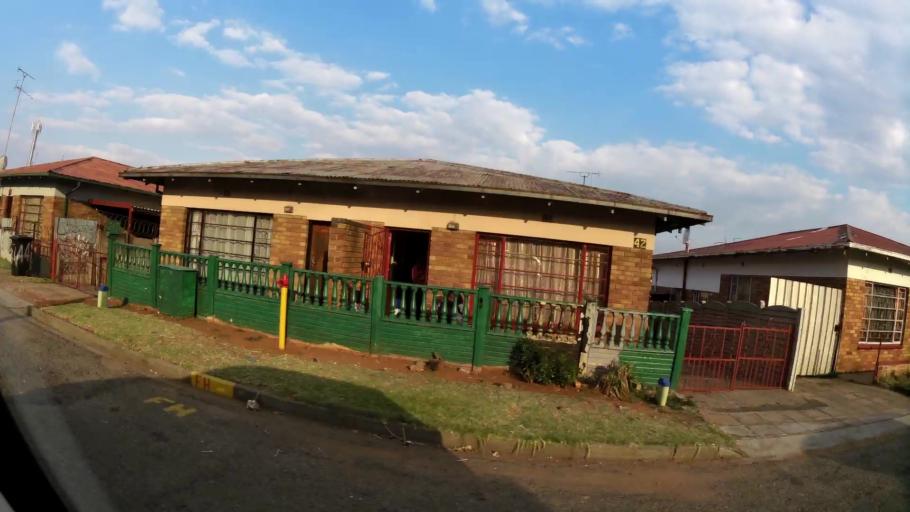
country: ZA
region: Gauteng
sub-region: Ekurhuleni Metropolitan Municipality
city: Germiston
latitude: -26.2450
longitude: 28.2037
